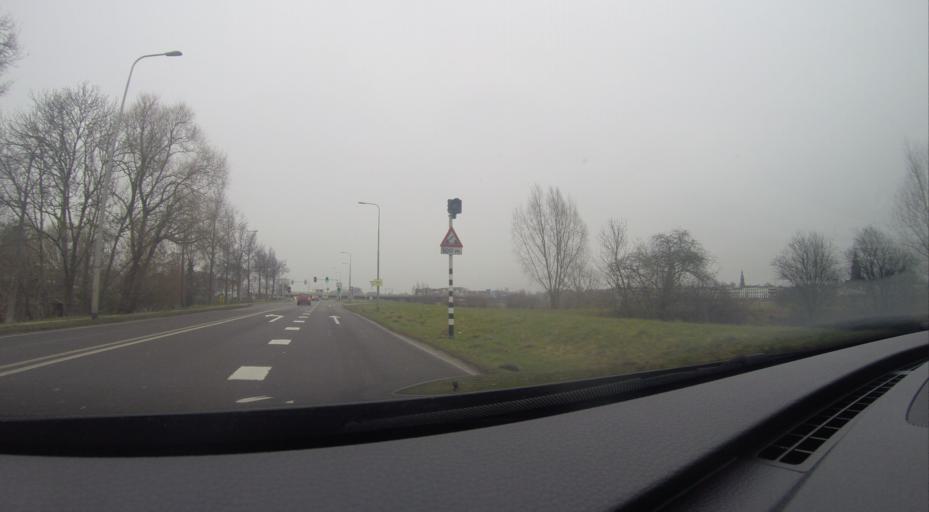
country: NL
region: Gelderland
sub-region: Gemeente Zutphen
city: Zutphen
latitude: 52.1397
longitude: 6.1840
